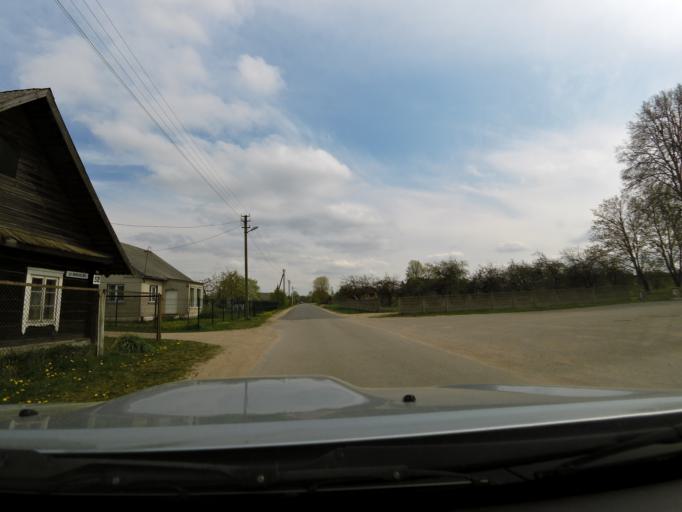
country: LT
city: Baltoji Voke
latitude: 54.4326
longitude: 25.1509
